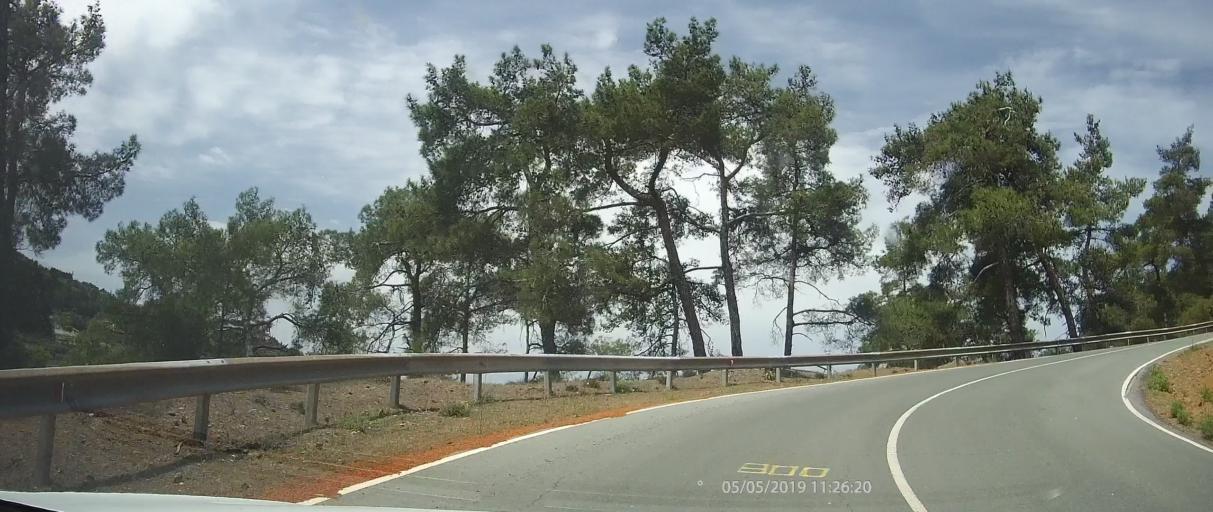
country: CY
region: Limassol
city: Pachna
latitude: 34.9277
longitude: 32.6470
